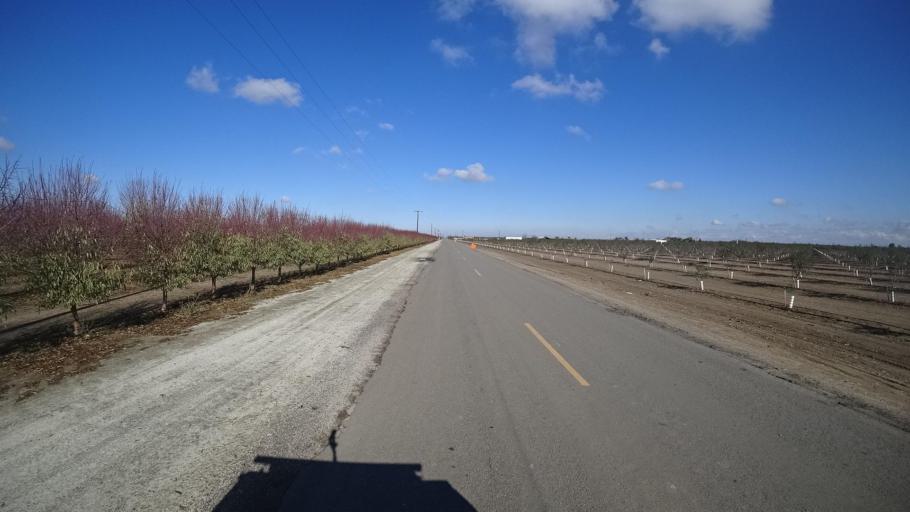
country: US
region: California
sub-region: Kern County
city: McFarland
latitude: 35.6637
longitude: -119.2588
